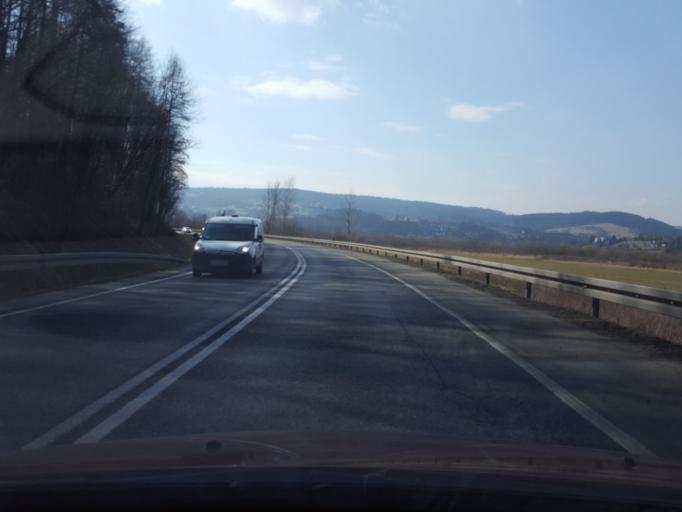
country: PL
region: Lesser Poland Voivodeship
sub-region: Powiat nowosadecki
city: Chelmiec
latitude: 49.6810
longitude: 20.6534
